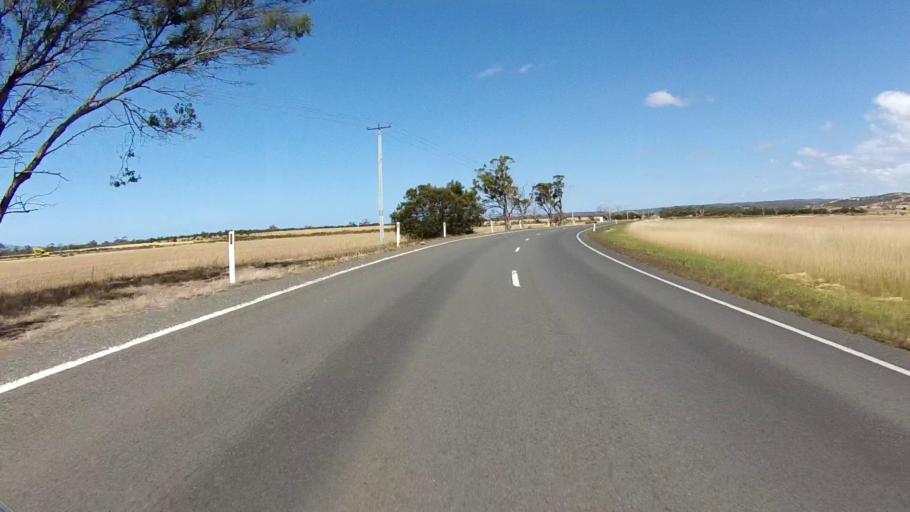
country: AU
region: Tasmania
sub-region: Break O'Day
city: St Helens
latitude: -42.0879
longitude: 148.0671
